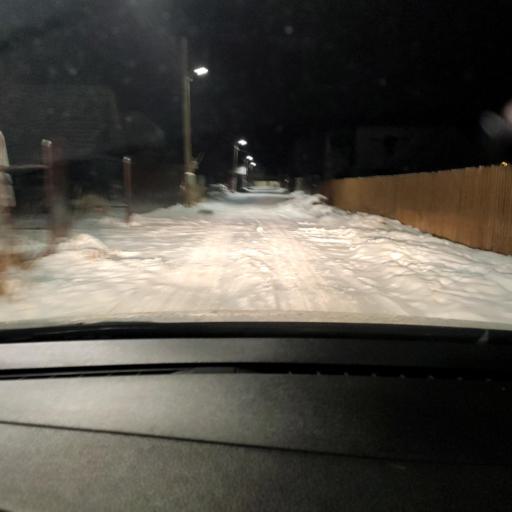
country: RU
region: Tatarstan
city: Stolbishchi
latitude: 55.7449
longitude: 49.2858
